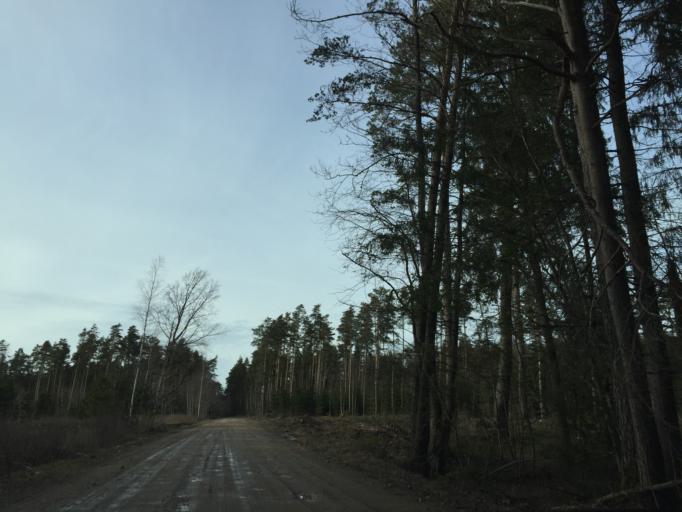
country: EE
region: Paernumaa
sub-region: Paernu linn
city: Parnu
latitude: 58.2167
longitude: 24.4952
